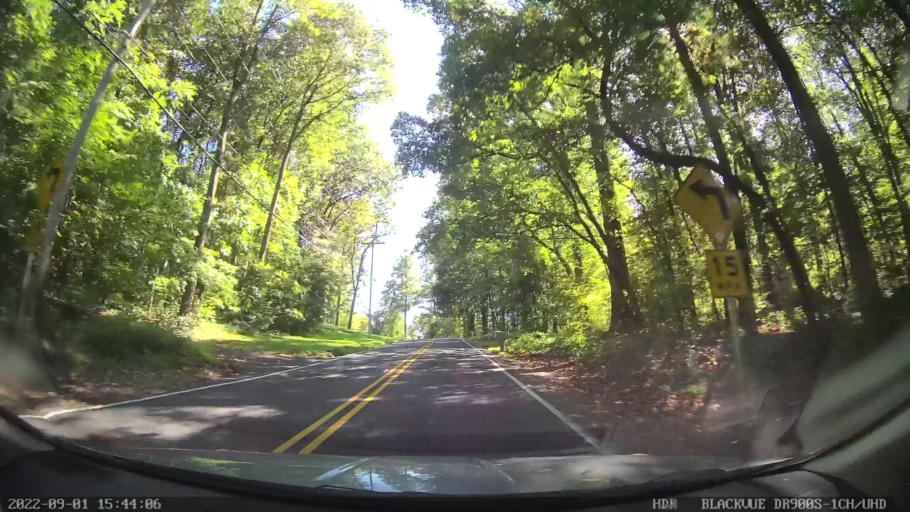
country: US
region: Pennsylvania
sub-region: Berks County
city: Topton
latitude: 40.4749
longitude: -75.7005
